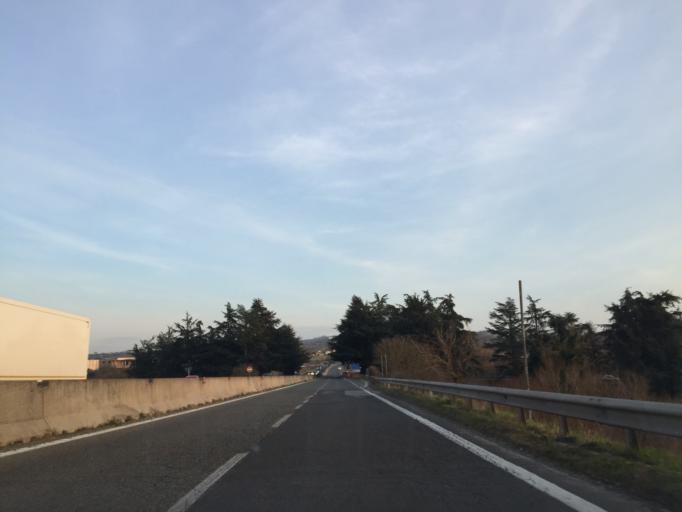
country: IT
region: Latium
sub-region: Citta metropolitana di Roma Capitale
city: Campagnano di Roma
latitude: 42.1557
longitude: 12.3436
